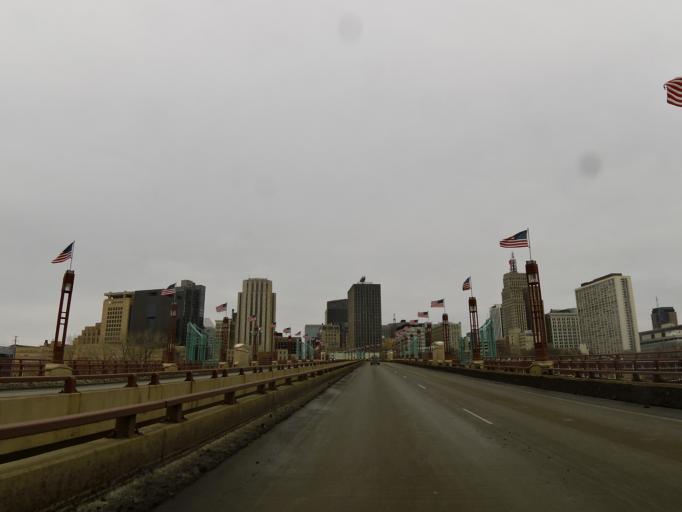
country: US
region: Minnesota
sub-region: Ramsey County
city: Saint Paul
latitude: 44.9408
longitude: -93.0905
